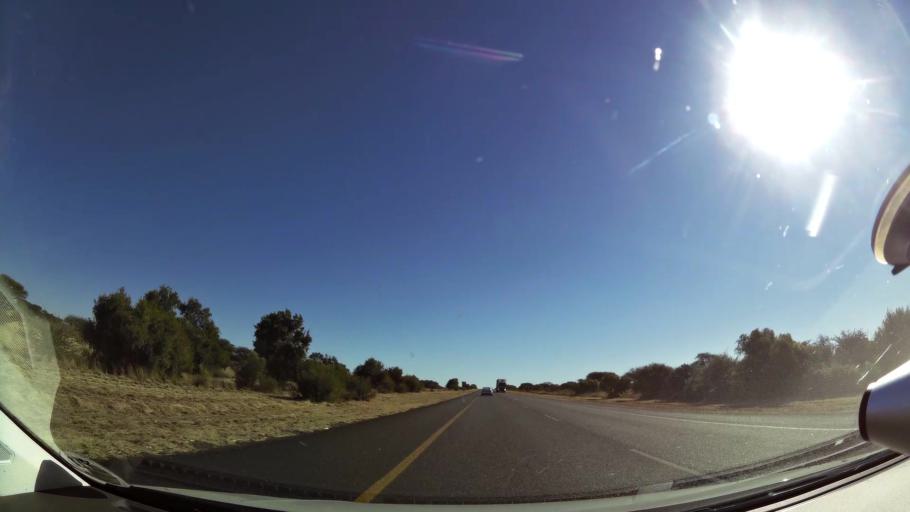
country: ZA
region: Northern Cape
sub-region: Frances Baard District Municipality
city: Warrenton
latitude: -28.2100
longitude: 24.8460
